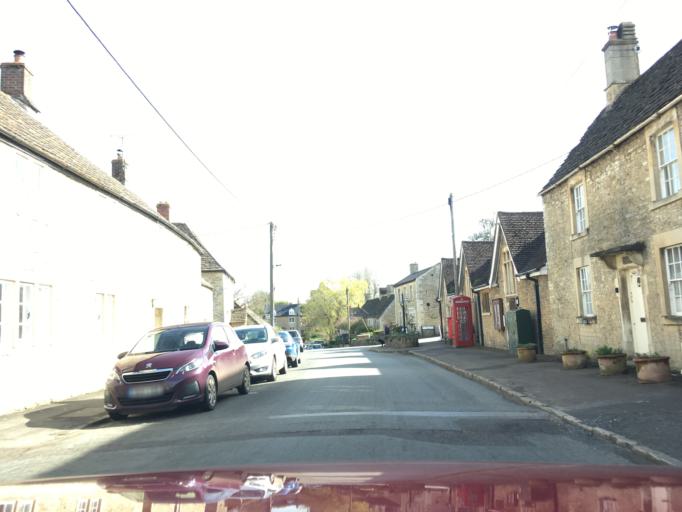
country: GB
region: England
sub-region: Wiltshire
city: Chippenham
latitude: 51.4945
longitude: -2.1391
